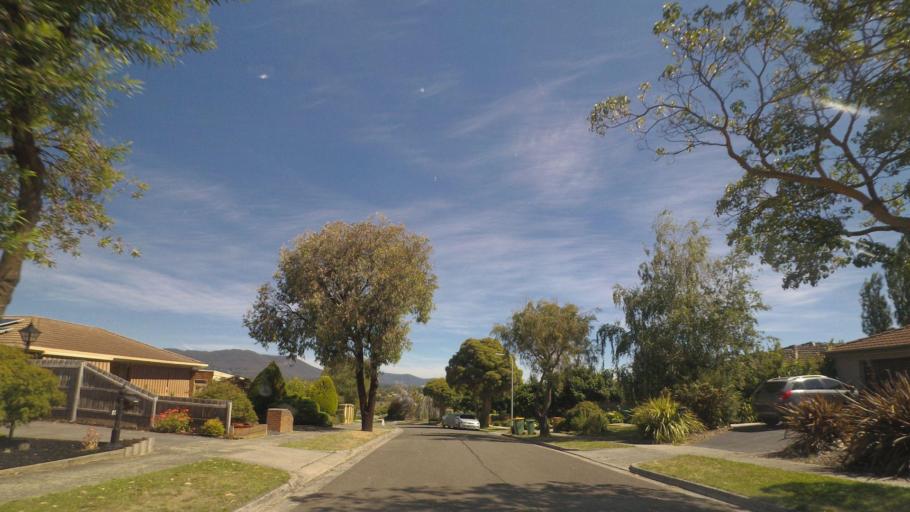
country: AU
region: Victoria
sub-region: Yarra Ranges
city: Lilydale
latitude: -37.7675
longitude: 145.3294
